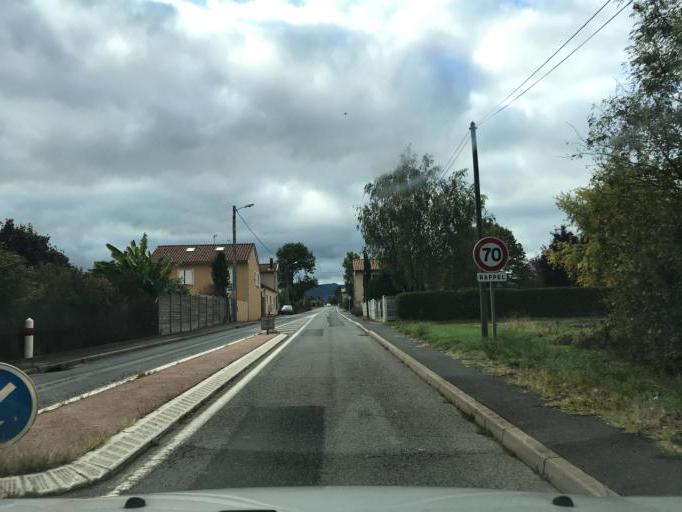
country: FR
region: Rhone-Alpes
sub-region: Departement du Rhone
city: Gleize
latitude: 45.9946
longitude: 4.6771
